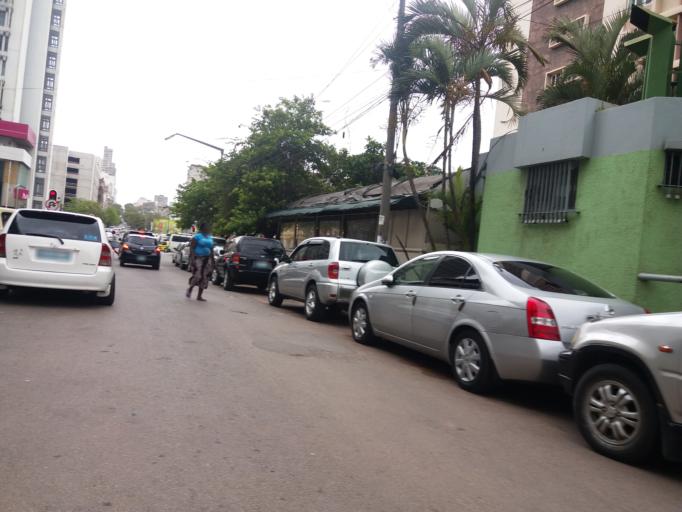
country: MZ
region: Maputo City
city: Maputo
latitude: -25.9722
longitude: 32.5690
